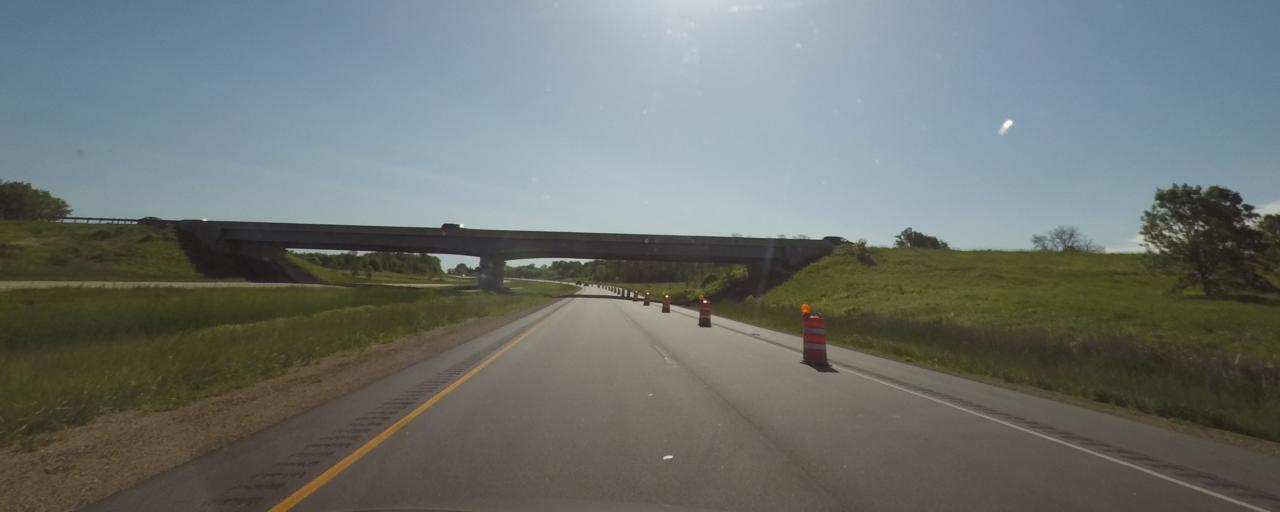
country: US
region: Wisconsin
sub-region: Columbia County
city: Columbus
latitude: 43.3575
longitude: -88.9961
